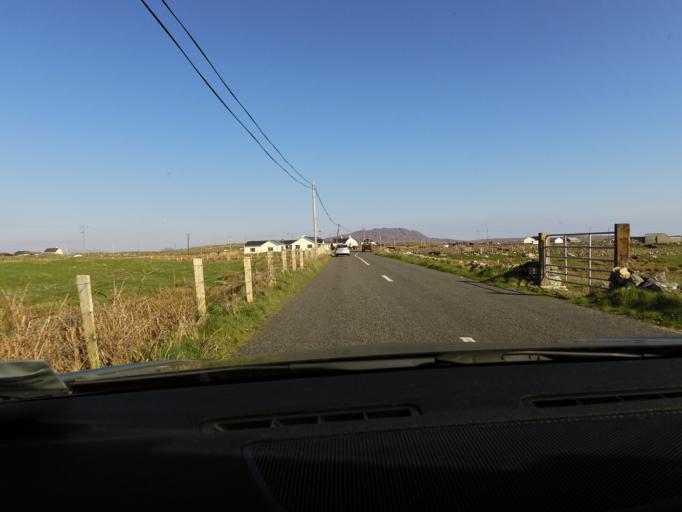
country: IE
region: Connaught
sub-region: County Galway
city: Clifden
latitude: 53.4156
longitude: -10.0517
